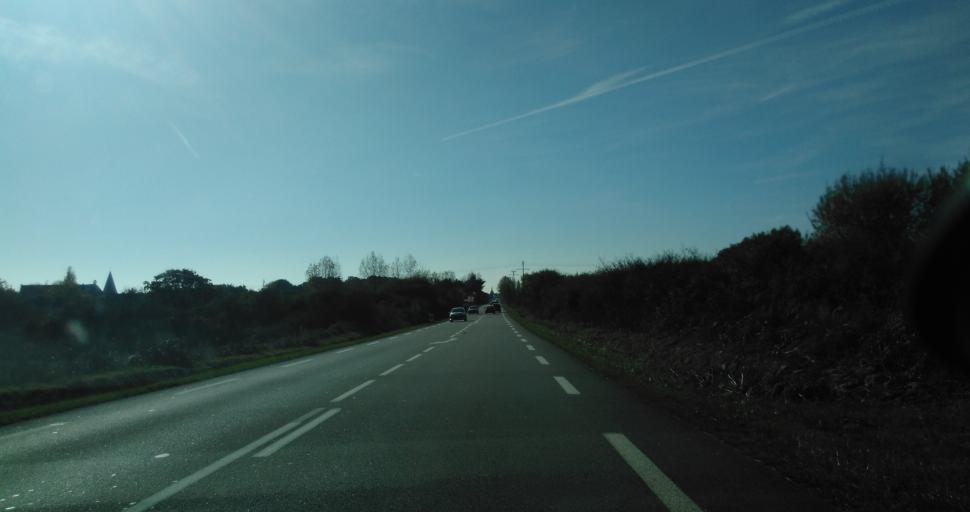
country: FR
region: Brittany
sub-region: Departement du Morbihan
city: Plouharnel
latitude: 47.6074
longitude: -3.0985
